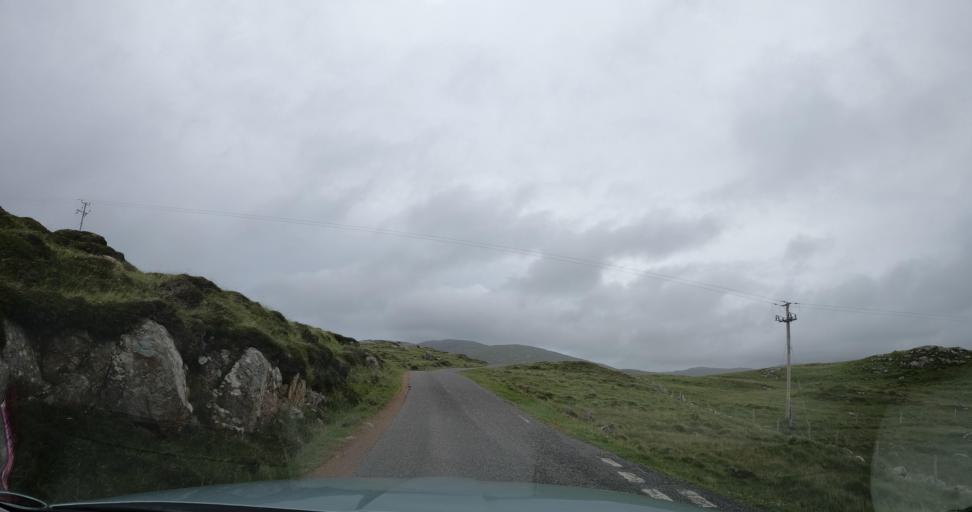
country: GB
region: Scotland
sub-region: Eilean Siar
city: Barra
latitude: 56.9342
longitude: -7.5184
